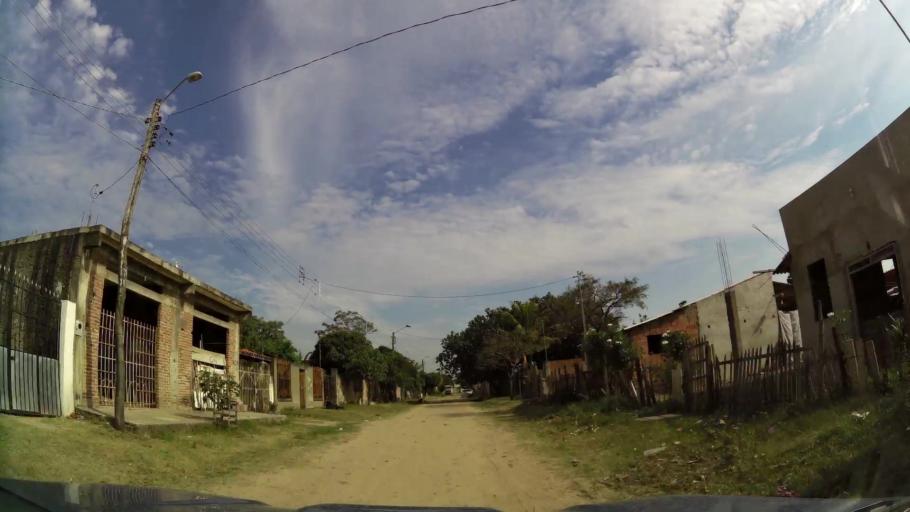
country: BO
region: Santa Cruz
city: Santa Cruz de la Sierra
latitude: -17.7342
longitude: -63.1355
